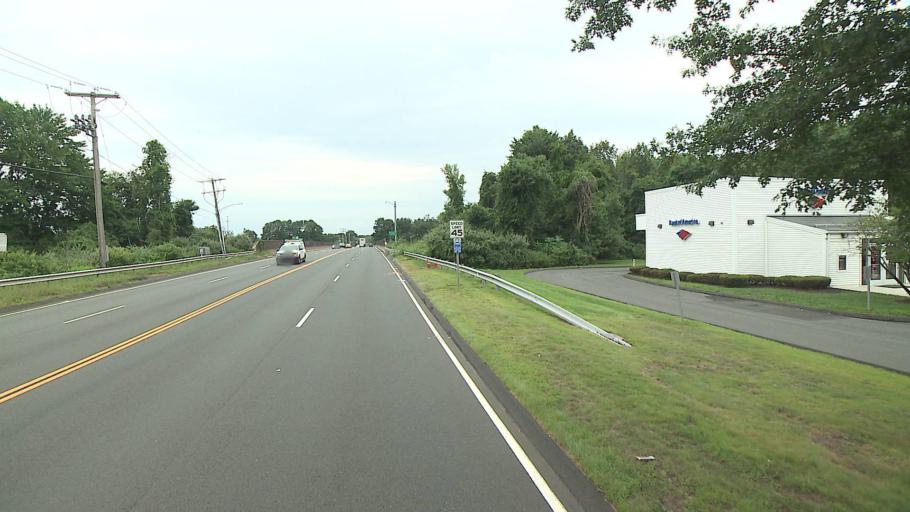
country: US
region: Connecticut
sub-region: Middlesex County
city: Cromwell
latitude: 41.6443
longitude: -72.6776
